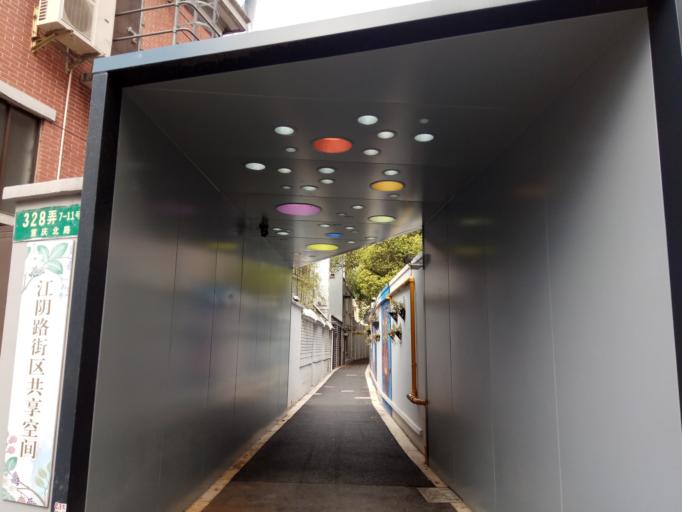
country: CN
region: Shanghai Shi
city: Shanghai
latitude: 31.2313
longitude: 121.4664
